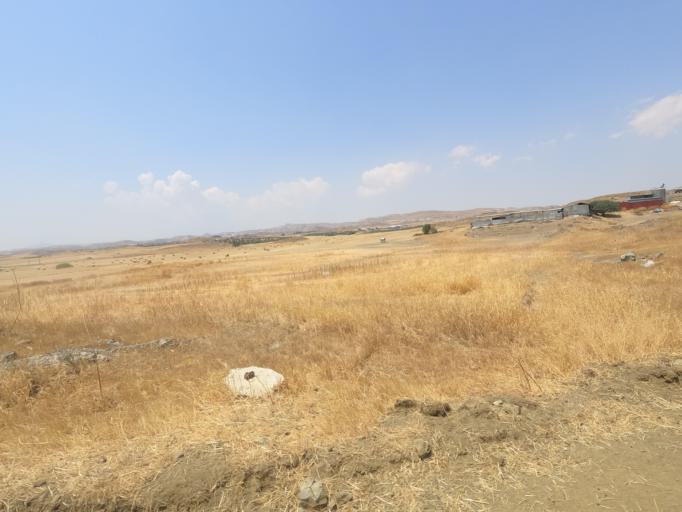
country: CY
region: Larnaka
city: Troulloi
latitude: 35.0171
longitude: 33.6044
